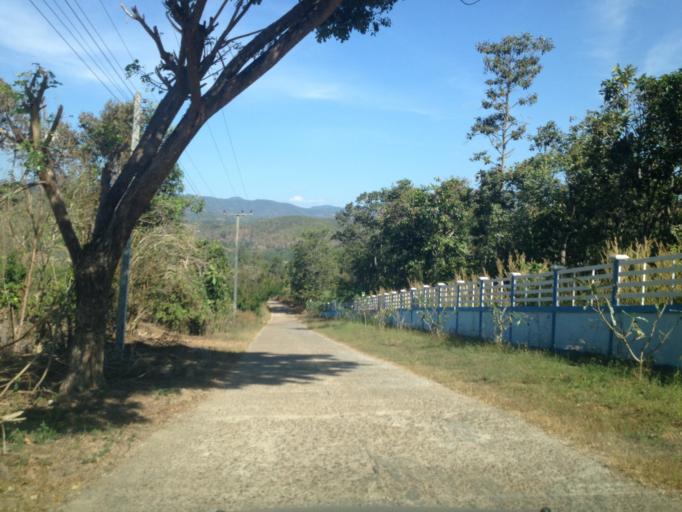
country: TH
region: Mae Hong Son
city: Ban Huai I Huak
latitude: 18.0838
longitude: 98.2030
